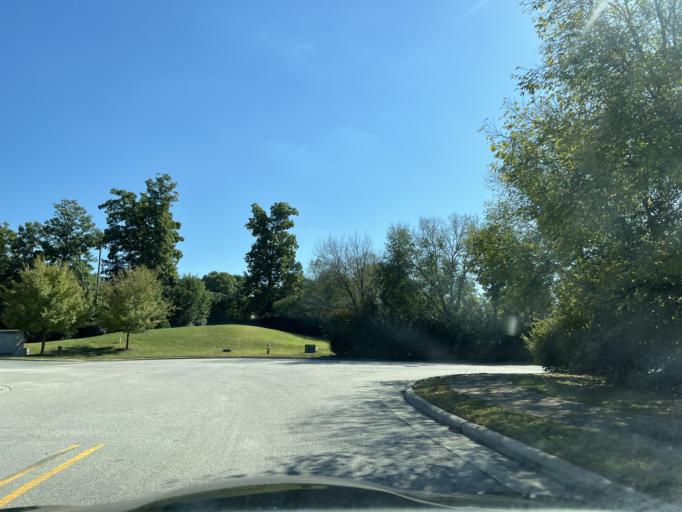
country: US
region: North Carolina
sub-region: Wake County
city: Garner
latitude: 35.7190
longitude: -78.6622
